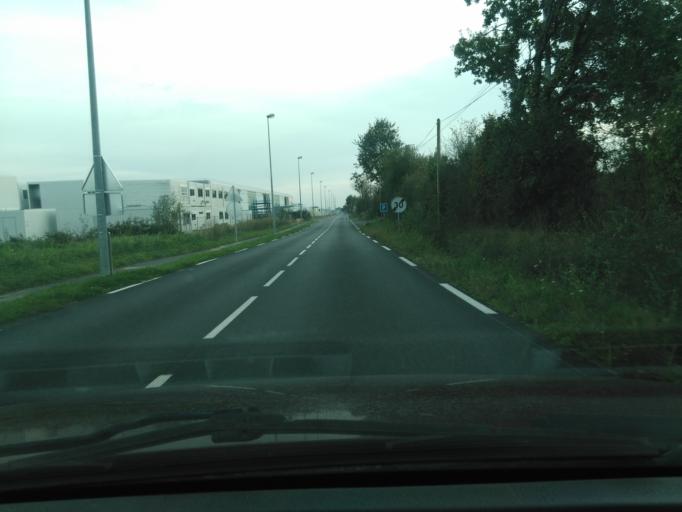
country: FR
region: Pays de la Loire
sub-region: Departement de la Vendee
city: Mouilleron-le-Captif
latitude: 46.7241
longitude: -1.4324
